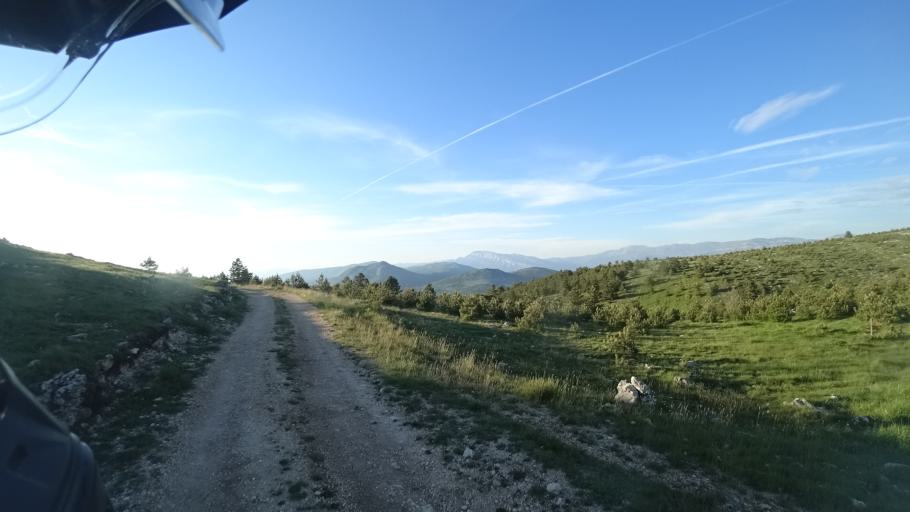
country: HR
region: Sibensko-Kniniska
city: Drnis
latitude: 43.8771
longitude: 16.3488
